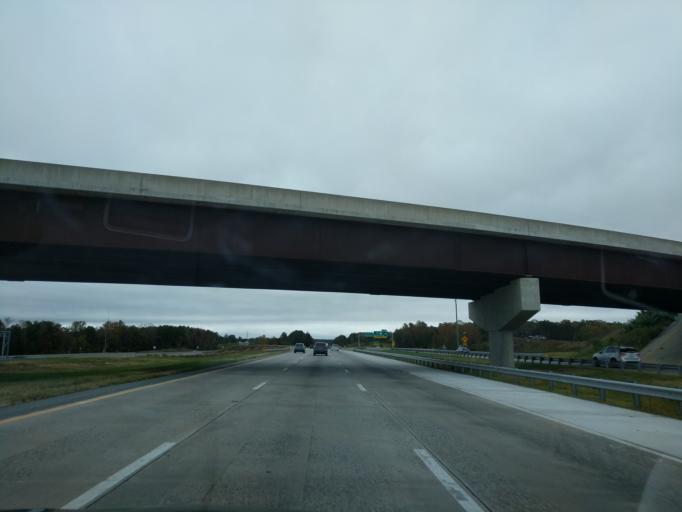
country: US
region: North Carolina
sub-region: Randolph County
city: Archdale
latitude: 35.9277
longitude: -79.9265
